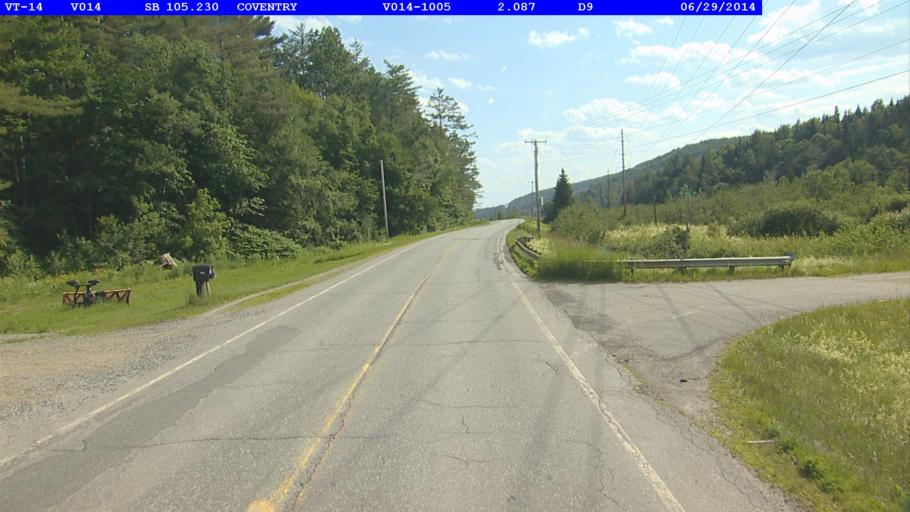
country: US
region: Vermont
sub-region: Orleans County
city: Newport
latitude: 44.8931
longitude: -72.2586
